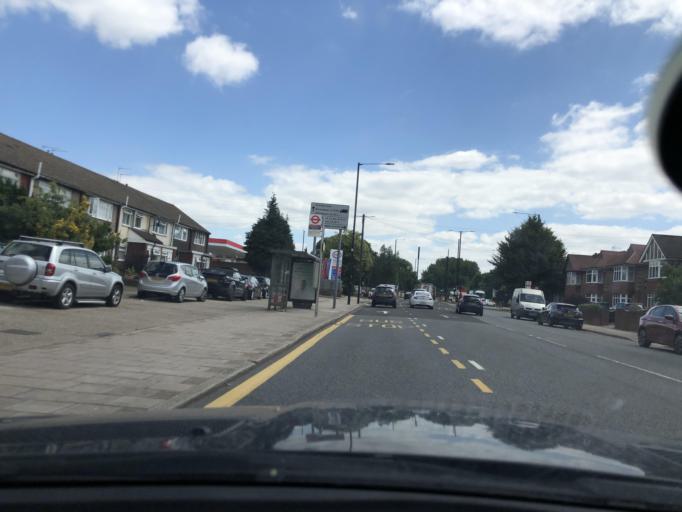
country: GB
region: England
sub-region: Hertfordshire
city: Waltham Cross
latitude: 51.6804
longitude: -0.0358
